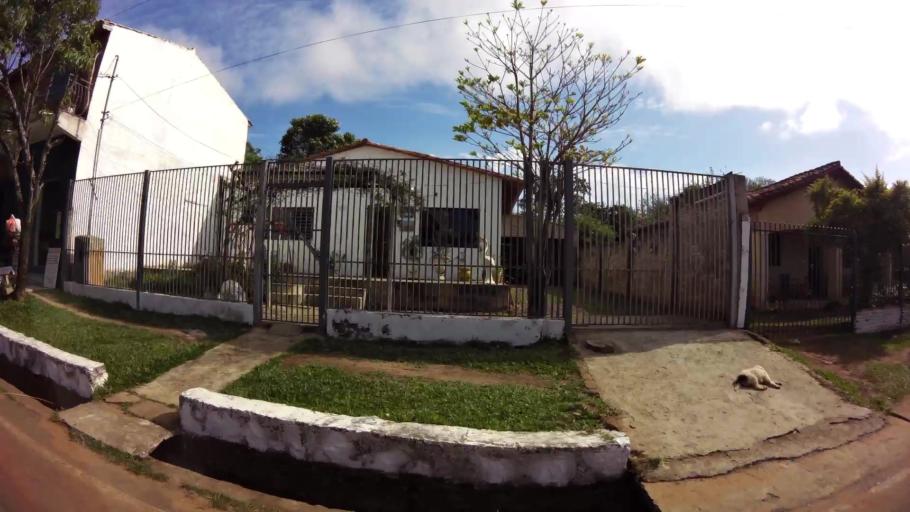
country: PY
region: Central
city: San Lorenzo
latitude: -25.2808
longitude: -57.4879
